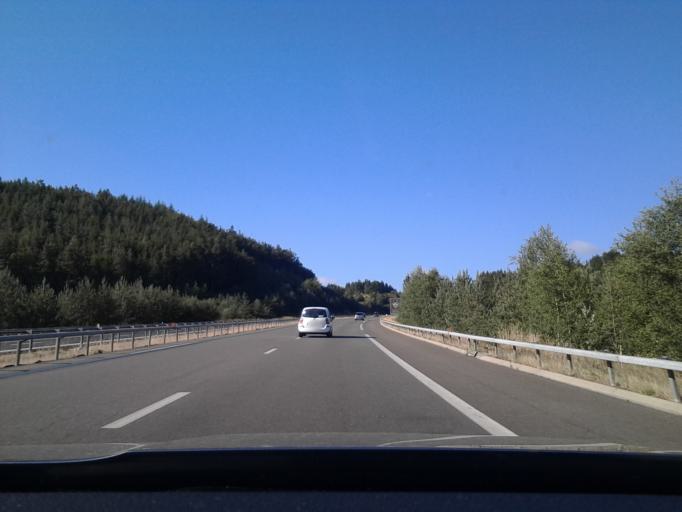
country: FR
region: Languedoc-Roussillon
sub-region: Departement de la Lozere
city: Aumont-Aubrac
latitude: 44.6626
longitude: 3.2588
